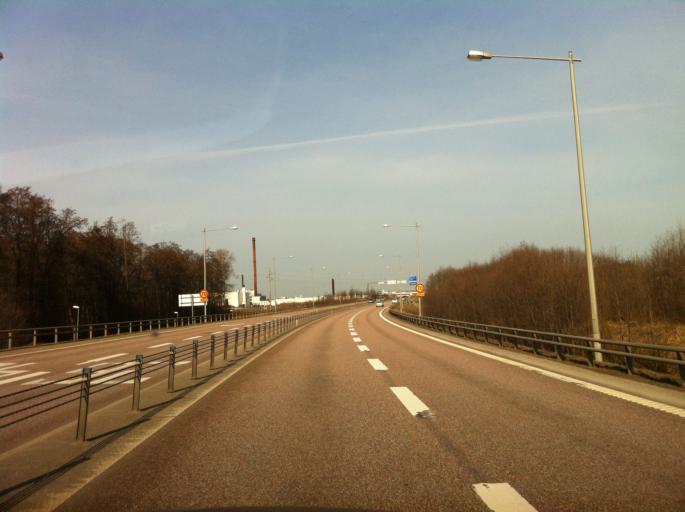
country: SE
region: Vaestra Goetaland
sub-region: Skovde Kommun
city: Skoevde
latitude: 58.3703
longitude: 13.8548
